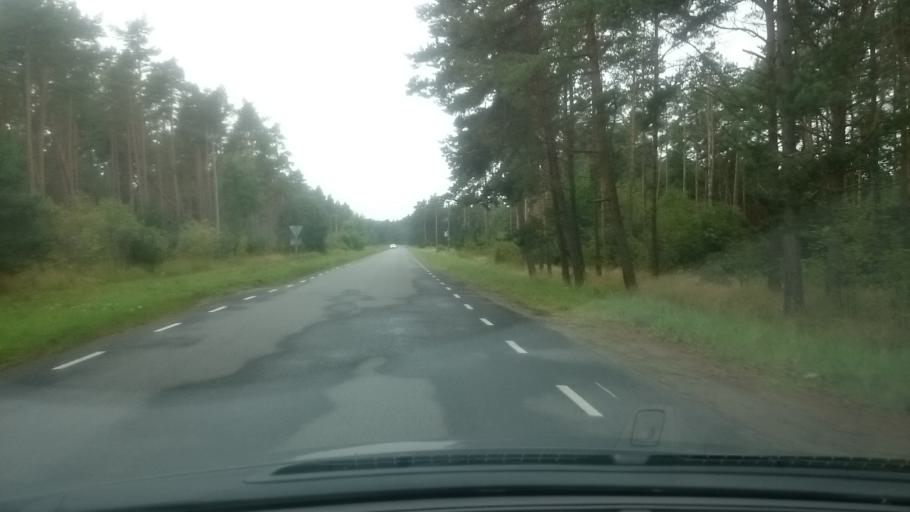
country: EE
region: Harju
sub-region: Raasiku vald
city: Raasiku
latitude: 59.5104
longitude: 25.2686
